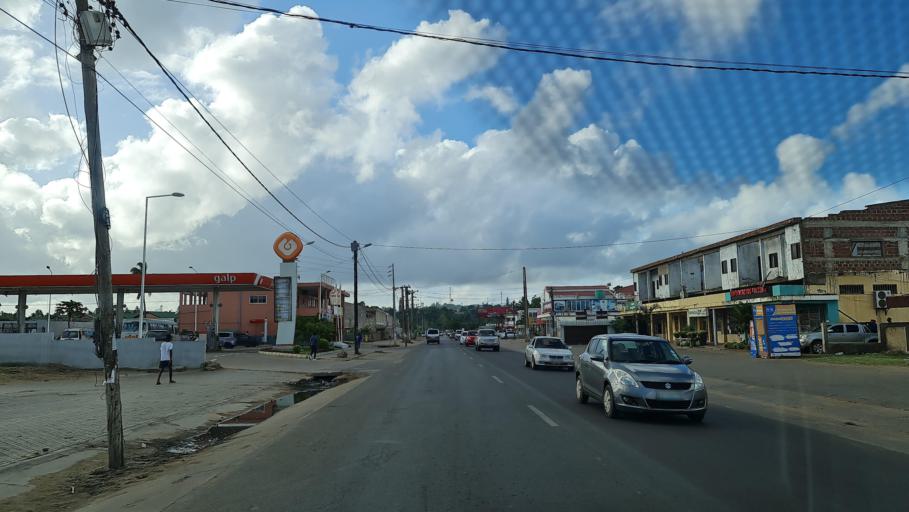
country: MZ
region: Gaza
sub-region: Xai-Xai District
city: Xai-Xai
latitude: -25.0502
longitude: 33.6469
